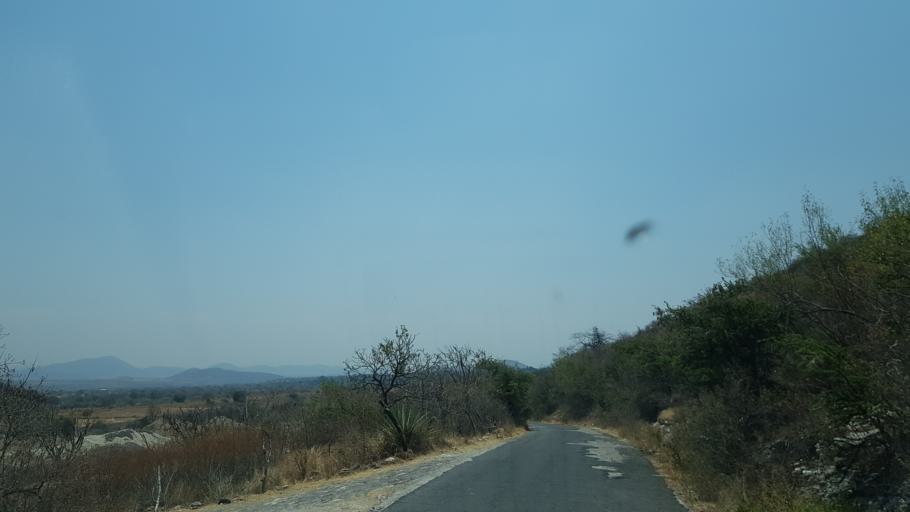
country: MX
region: Puebla
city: Huaquechula
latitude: 18.7908
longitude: -98.5441
